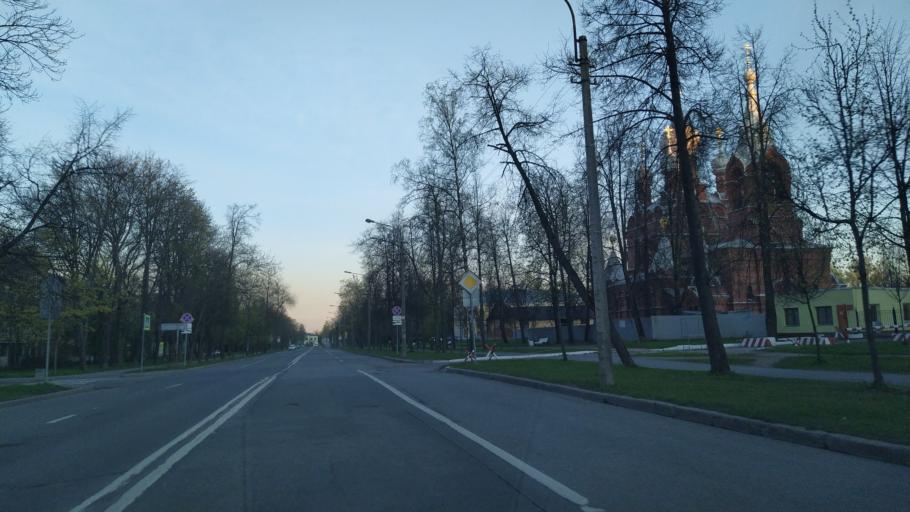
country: RU
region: St.-Petersburg
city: Pushkin
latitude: 59.7074
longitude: 30.4043
